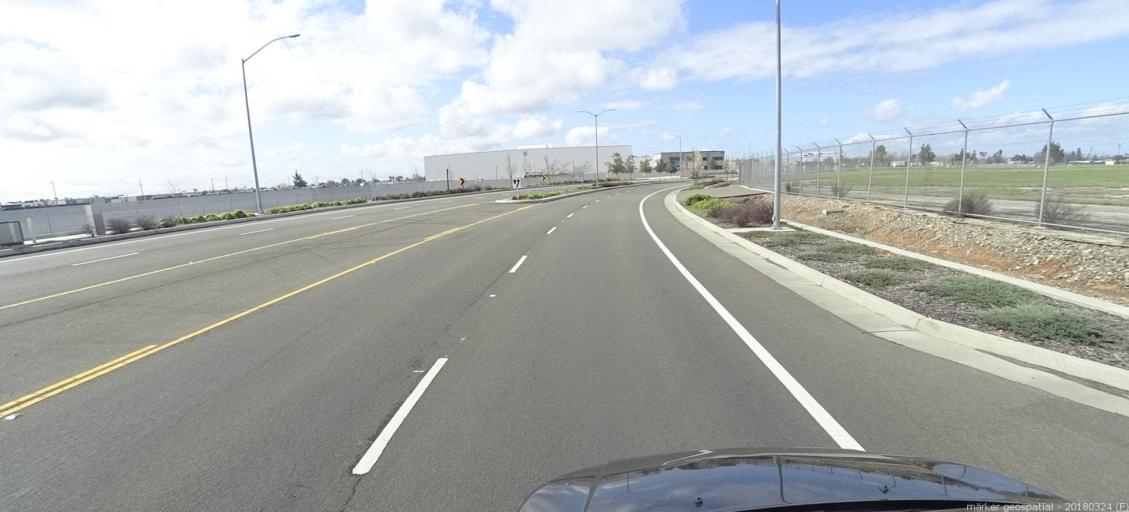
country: US
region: California
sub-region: Sacramento County
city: North Highlands
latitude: 38.6479
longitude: -121.3982
